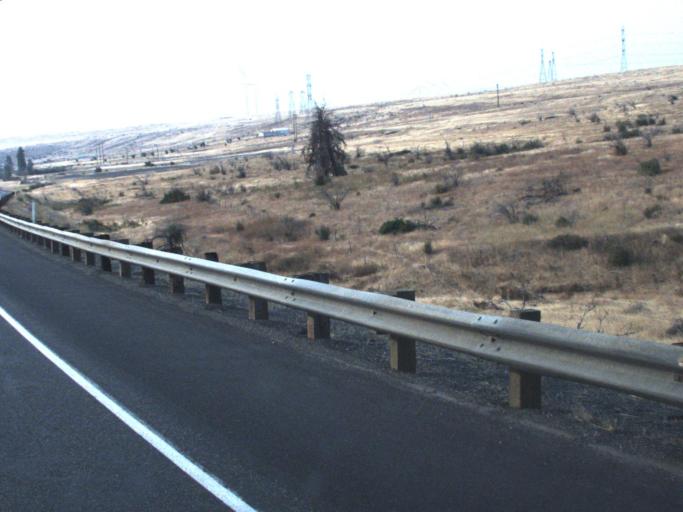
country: US
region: Washington
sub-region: Kittitas County
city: Ellensburg
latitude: 47.1443
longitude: -120.6915
